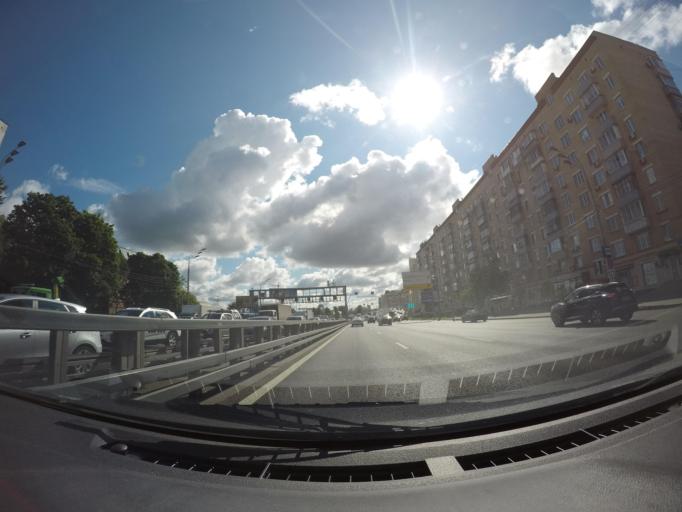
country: RU
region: Moscow
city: Mar'ina Roshcha
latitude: 55.7930
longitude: 37.6264
